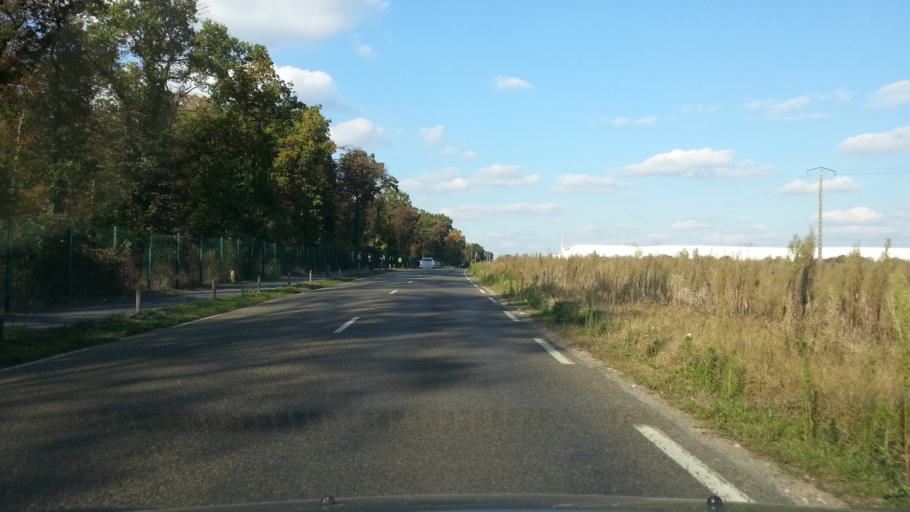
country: FR
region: Picardie
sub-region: Departement de l'Oise
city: Saint-Maximin
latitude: 49.2281
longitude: 2.4566
